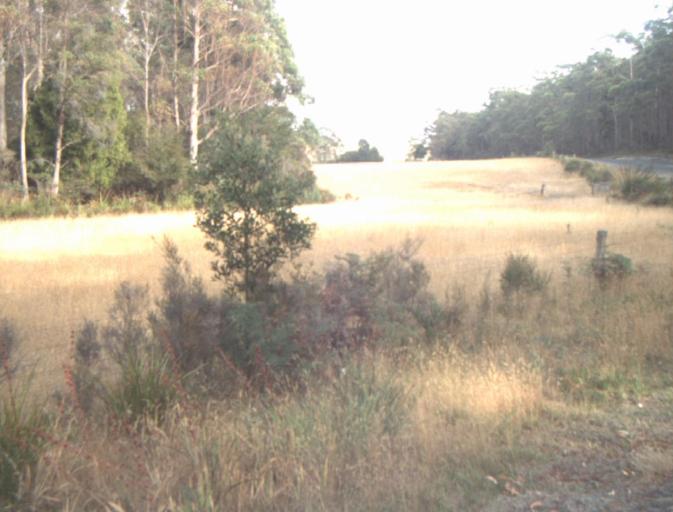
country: AU
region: Tasmania
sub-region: Dorset
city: Bridport
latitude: -41.1529
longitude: 147.2386
